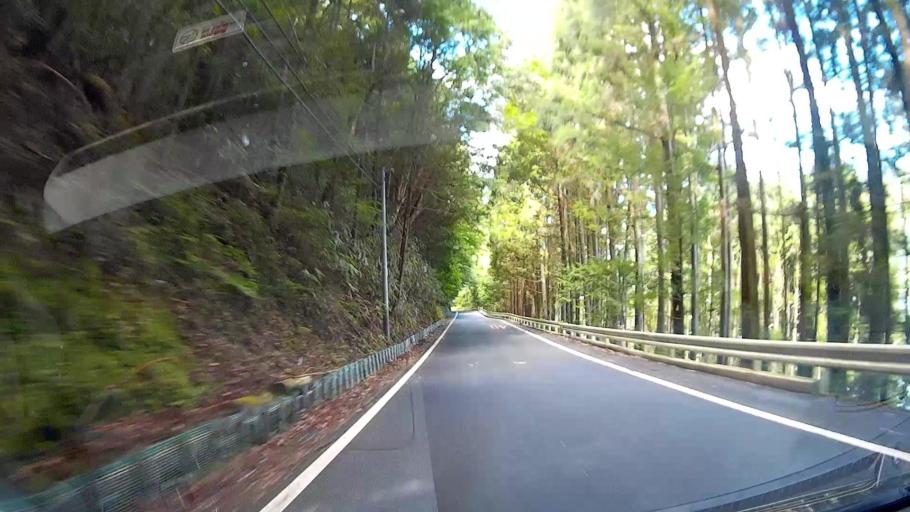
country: JP
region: Shizuoka
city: Shizuoka-shi
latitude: 35.2182
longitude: 138.2373
